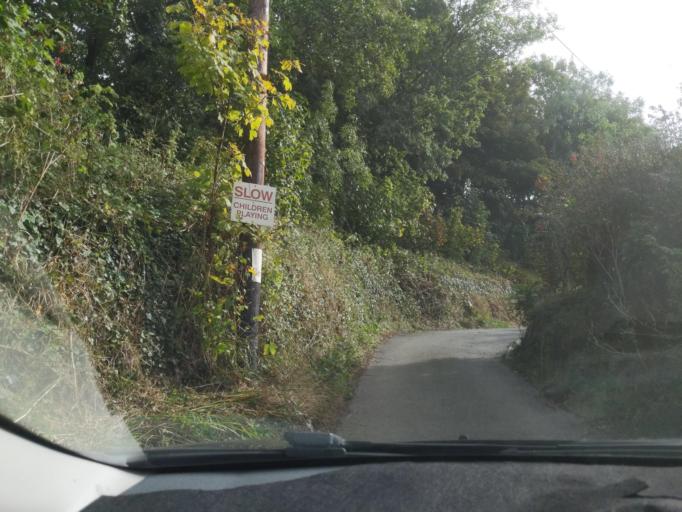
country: GB
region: England
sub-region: Cornwall
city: Mevagissey
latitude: 50.2390
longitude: -4.7895
